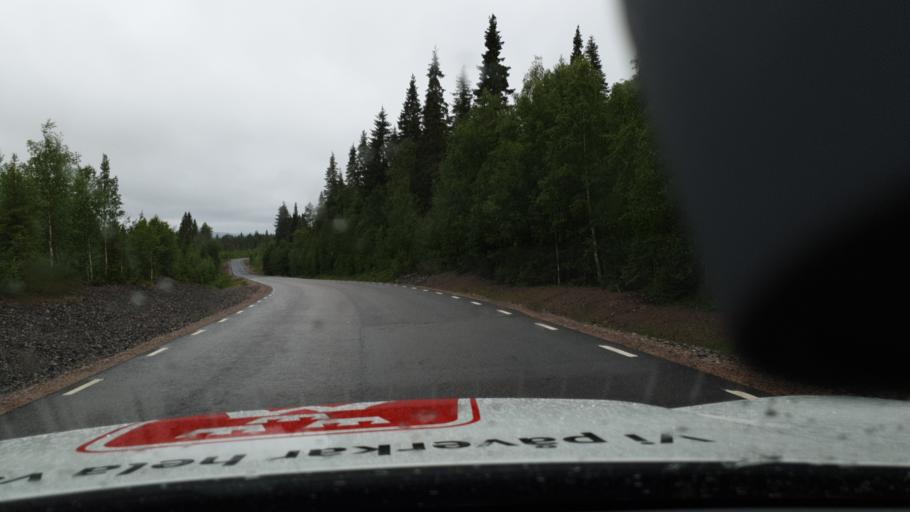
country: SE
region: Norrbotten
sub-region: Overtornea Kommun
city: OEvertornea
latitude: 66.5441
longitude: 23.3553
